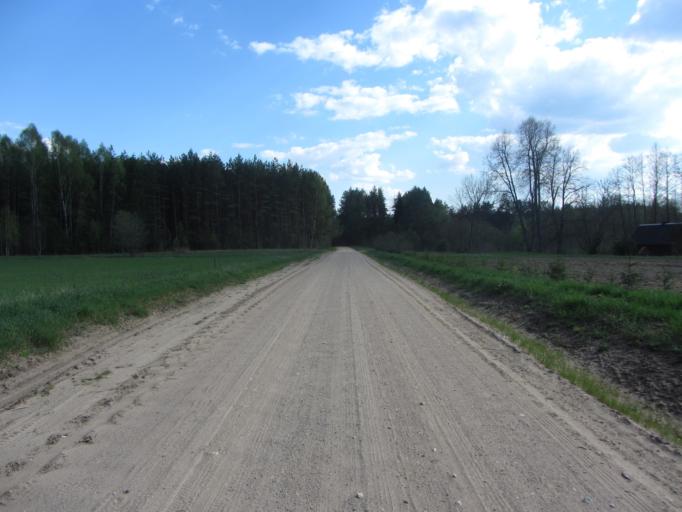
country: LT
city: Svencioneliai
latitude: 55.1818
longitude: 25.8290
